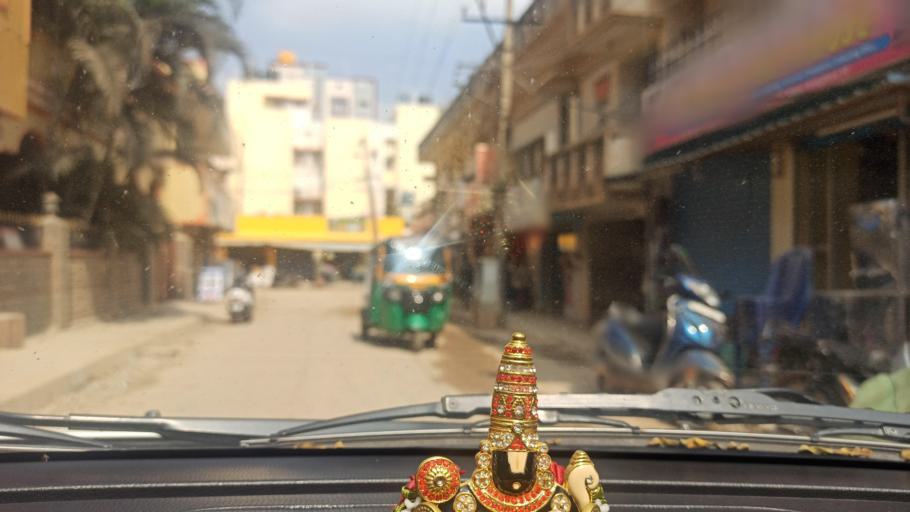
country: IN
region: Karnataka
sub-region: Bangalore Urban
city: Bangalore
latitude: 13.0165
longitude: 77.6655
